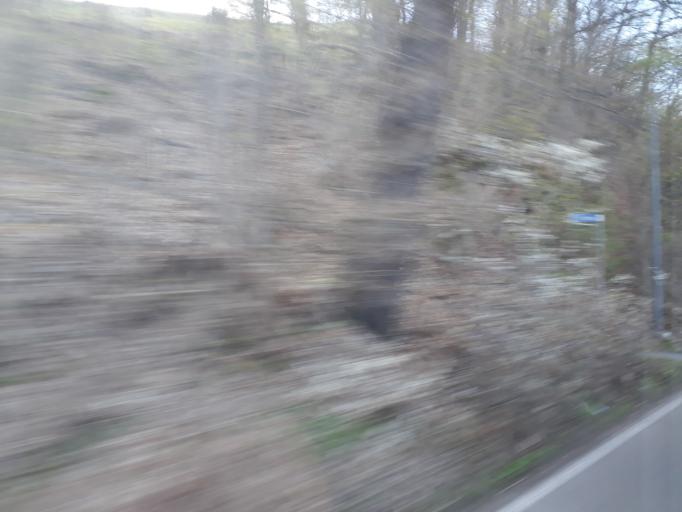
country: DE
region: Saxony
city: Kreischa
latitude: 50.9310
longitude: 13.7756
